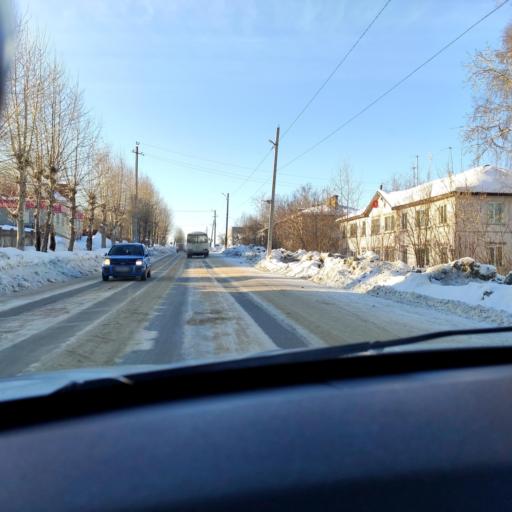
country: RU
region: Perm
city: Polazna
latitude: 58.2927
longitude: 56.4098
